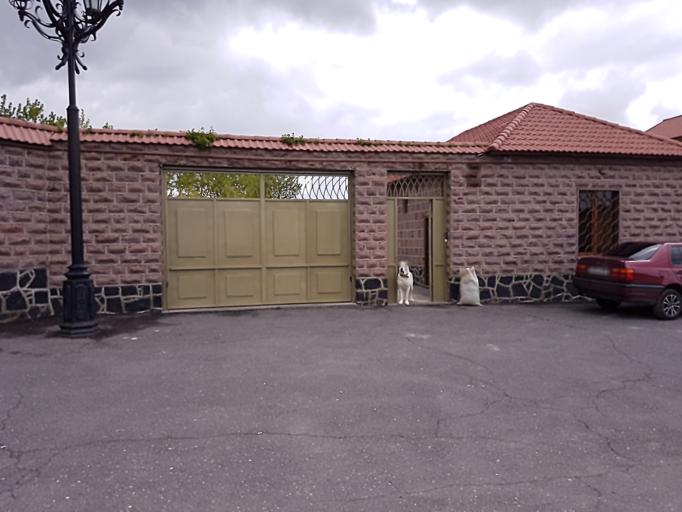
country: AM
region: Kotayk'i Marz
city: Dzoraghbyur
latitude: 40.1955
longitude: 44.6323
